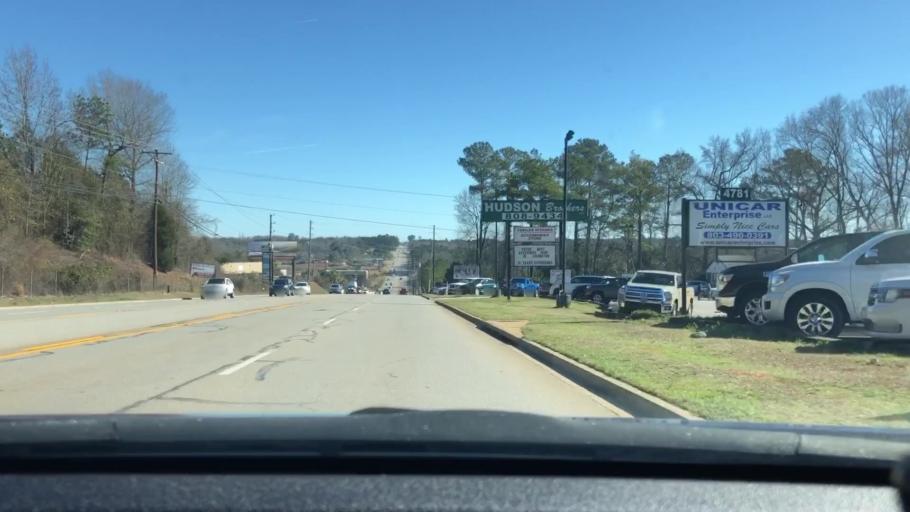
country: US
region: South Carolina
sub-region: Lexington County
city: Oak Grove
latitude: 34.0127
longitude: -81.1769
